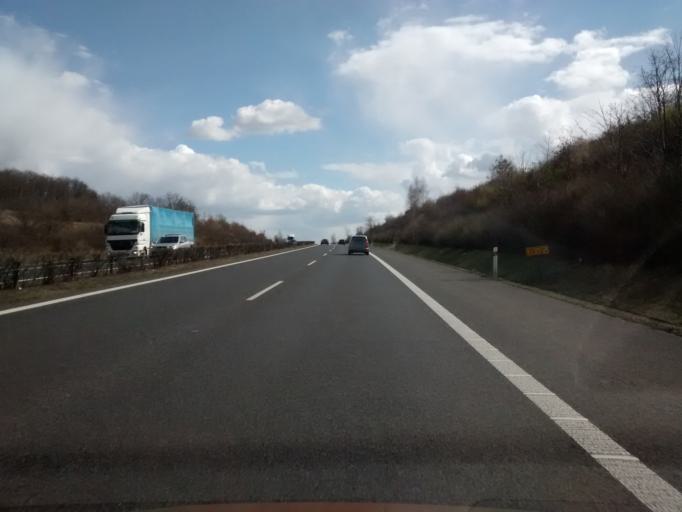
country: CZ
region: Ustecky
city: Roudnice nad Labem
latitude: 50.3678
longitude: 14.2572
